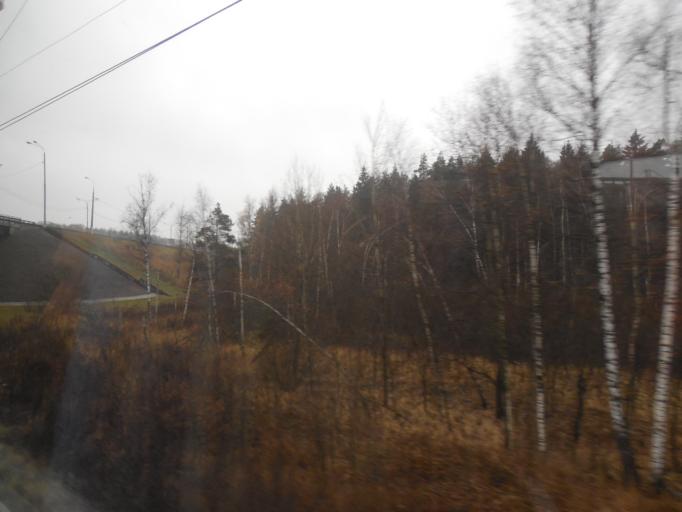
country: RU
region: Moskovskaya
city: Vostryakovo
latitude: 55.4131
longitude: 37.7920
